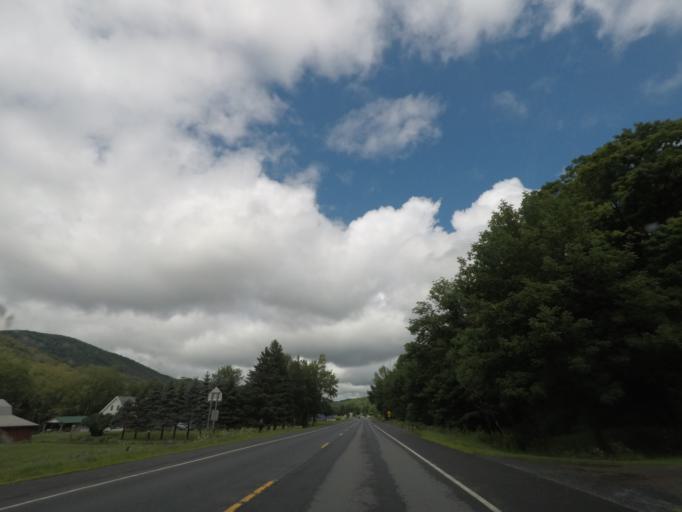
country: US
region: Massachusetts
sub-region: Berkshire County
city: Williamstown
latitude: 42.6404
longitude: -73.3597
